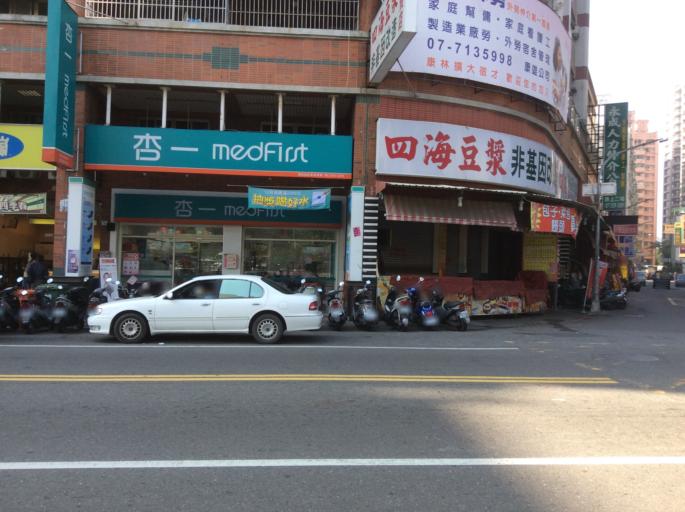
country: TW
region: Kaohsiung
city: Kaohsiung
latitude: 22.6788
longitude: 120.3220
